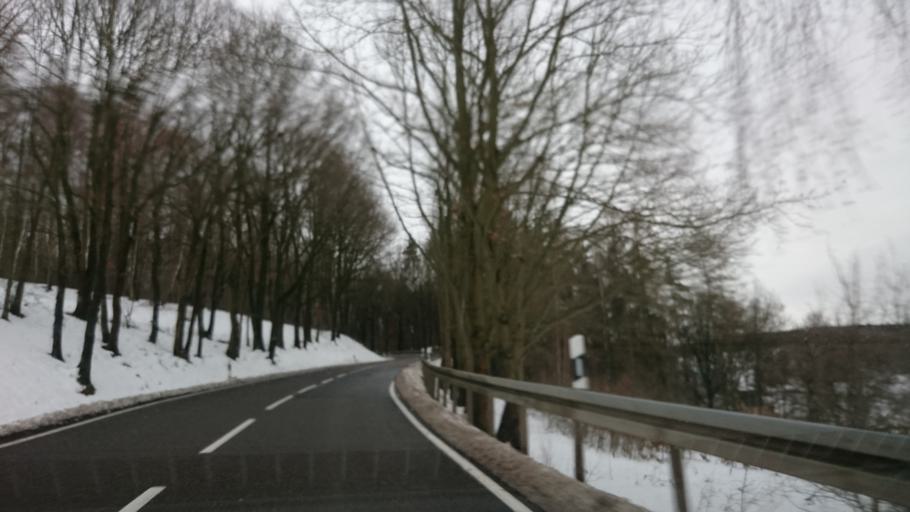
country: DE
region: Saxony
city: Sankt Egidien
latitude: 50.7759
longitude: 12.6189
